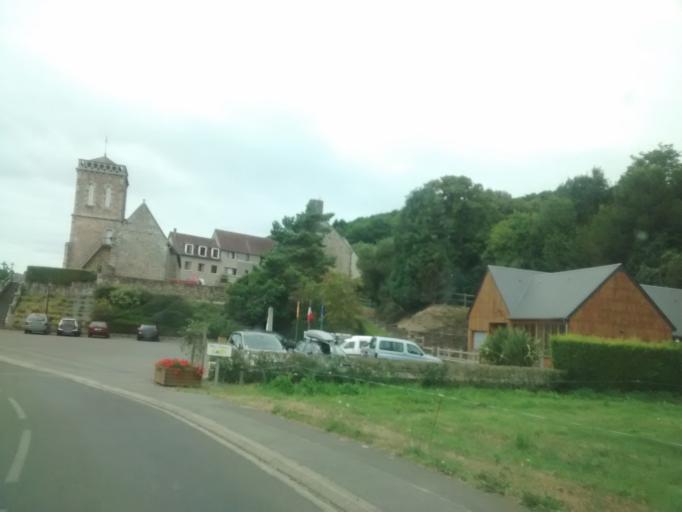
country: FR
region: Lower Normandy
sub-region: Departement de la Manche
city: Sartilly
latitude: 48.7302
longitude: -1.5124
